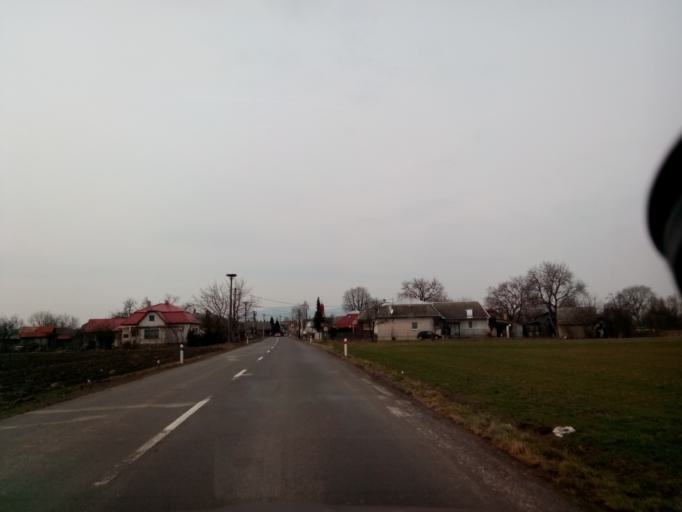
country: SK
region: Kosicky
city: Trebisov
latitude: 48.5968
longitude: 21.6319
